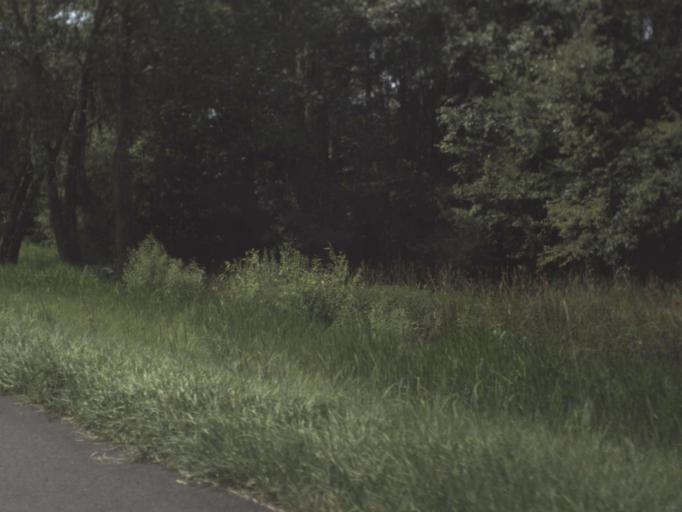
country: US
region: Florida
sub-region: Hamilton County
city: Jasper
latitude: 30.5851
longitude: -83.0022
